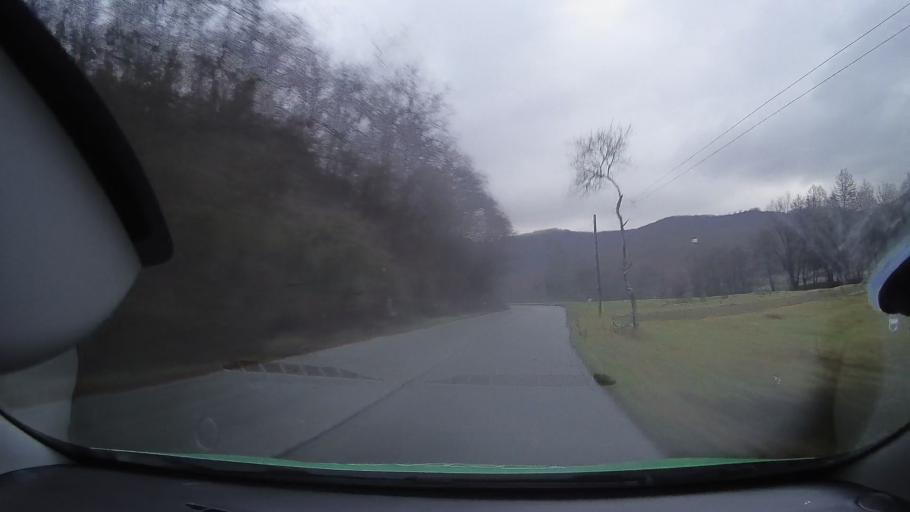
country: RO
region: Hunedoara
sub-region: Comuna Baia de Cris
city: Baia de Cris
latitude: 46.2022
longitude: 22.7182
